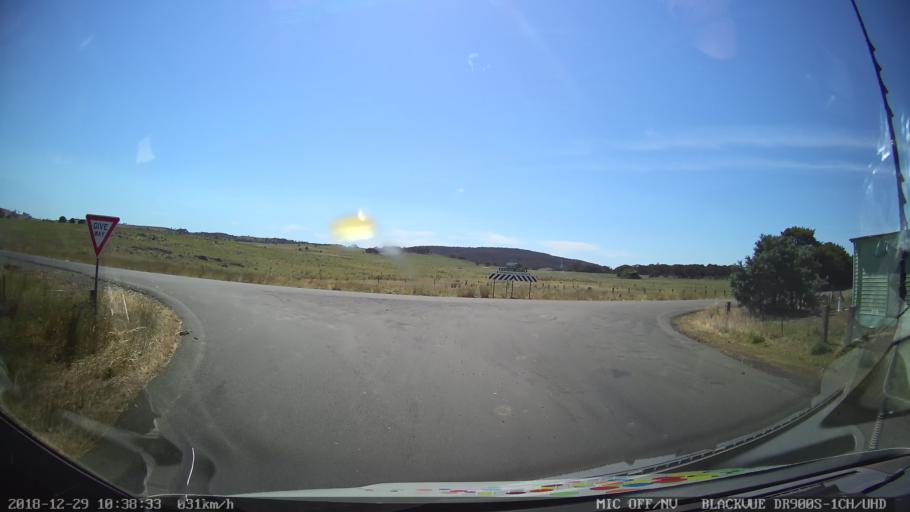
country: AU
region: New South Wales
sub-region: Yass Valley
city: Gundaroo
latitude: -35.0002
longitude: 149.5072
